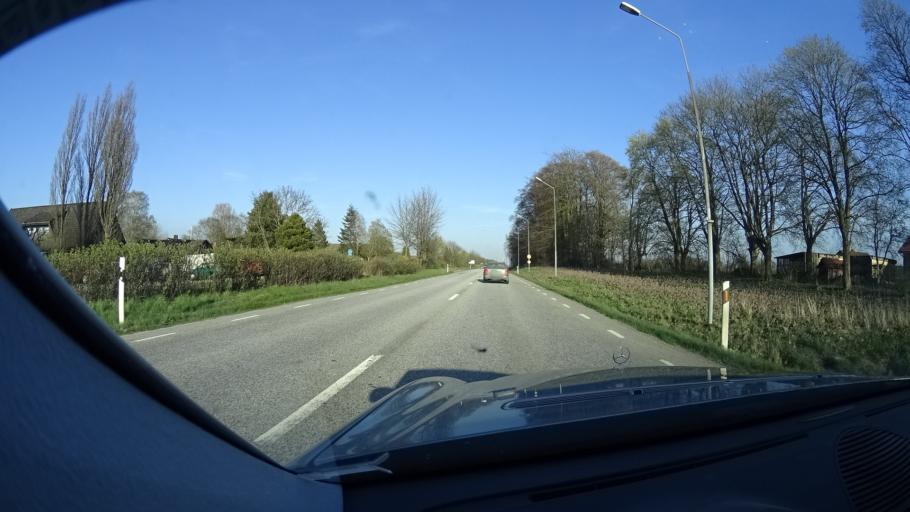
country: SE
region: Skane
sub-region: Eslovs Kommun
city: Stehag
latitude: 55.8517
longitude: 13.4084
